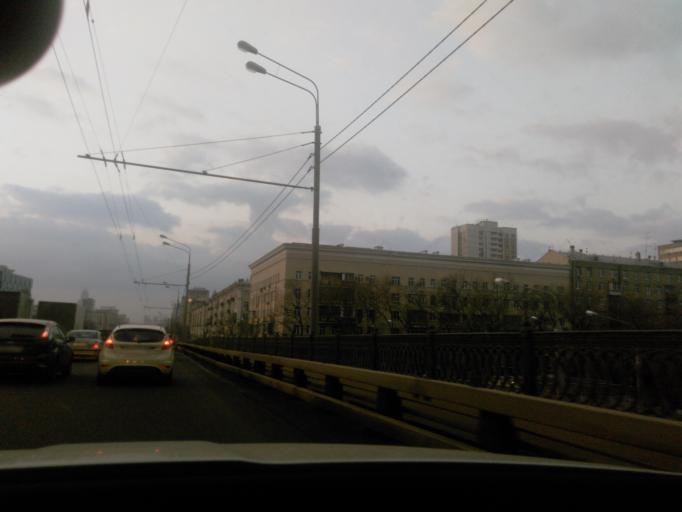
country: RU
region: Moskovskaya
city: Koptevo
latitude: 55.8243
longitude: 37.4933
